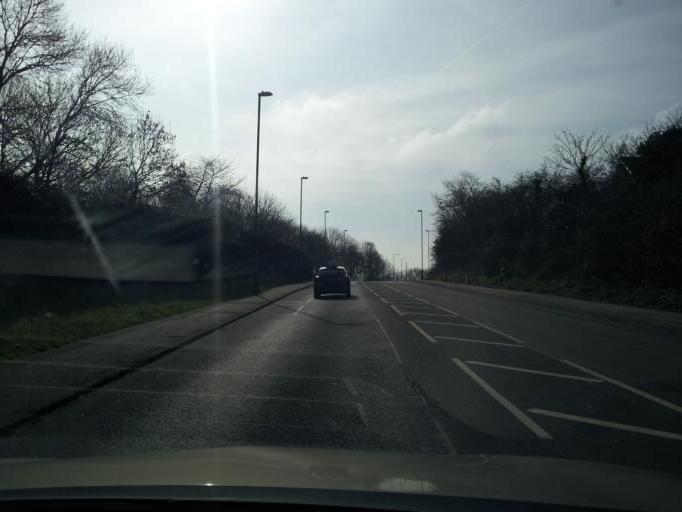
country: GB
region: England
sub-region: Nottinghamshire
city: Gotham
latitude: 52.8995
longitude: -1.1907
